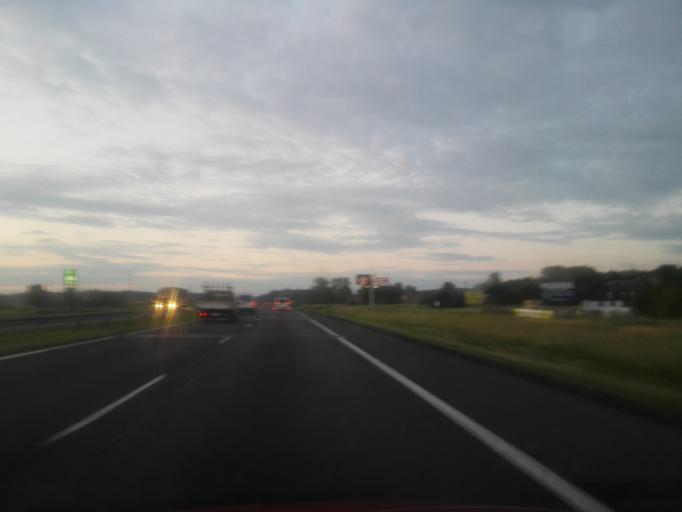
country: PL
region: Lodz Voivodeship
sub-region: Powiat radomszczanski
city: Kamiensk
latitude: 51.2335
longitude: 19.5147
